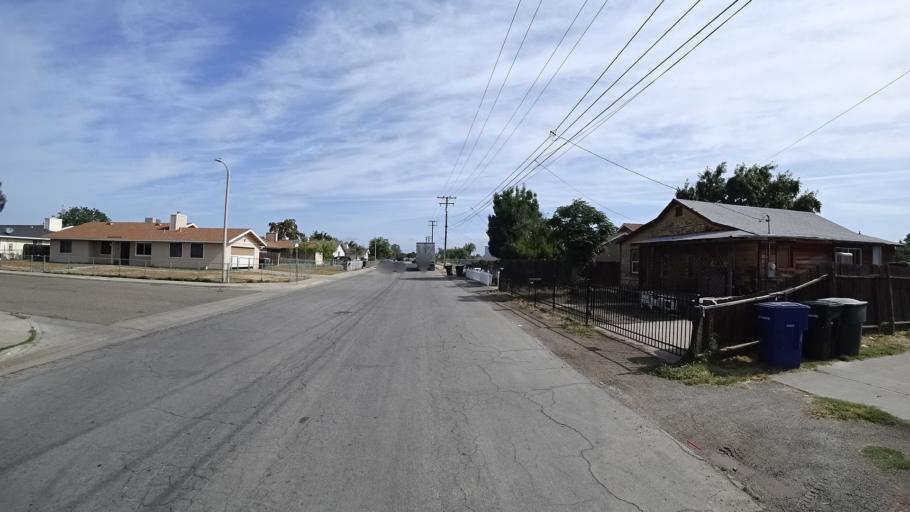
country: US
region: California
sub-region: Kings County
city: Hanford
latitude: 36.3182
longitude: -119.6617
